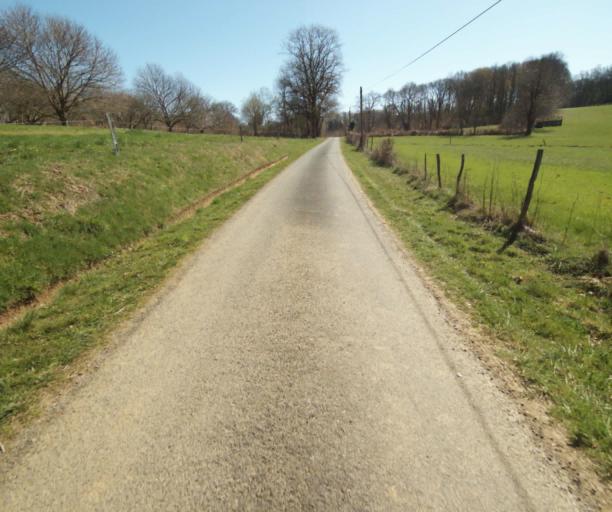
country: FR
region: Limousin
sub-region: Departement de la Correze
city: Saint-Clement
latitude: 45.3911
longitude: 1.6500
